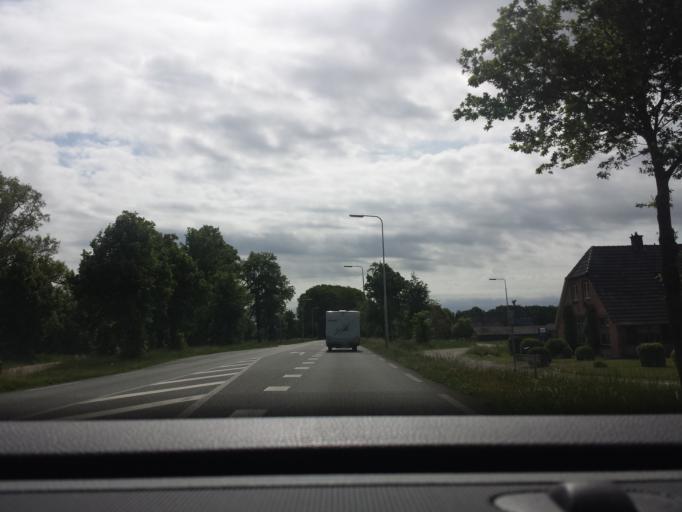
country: NL
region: Gelderland
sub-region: Berkelland
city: Borculo
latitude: 52.0672
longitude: 6.4852
